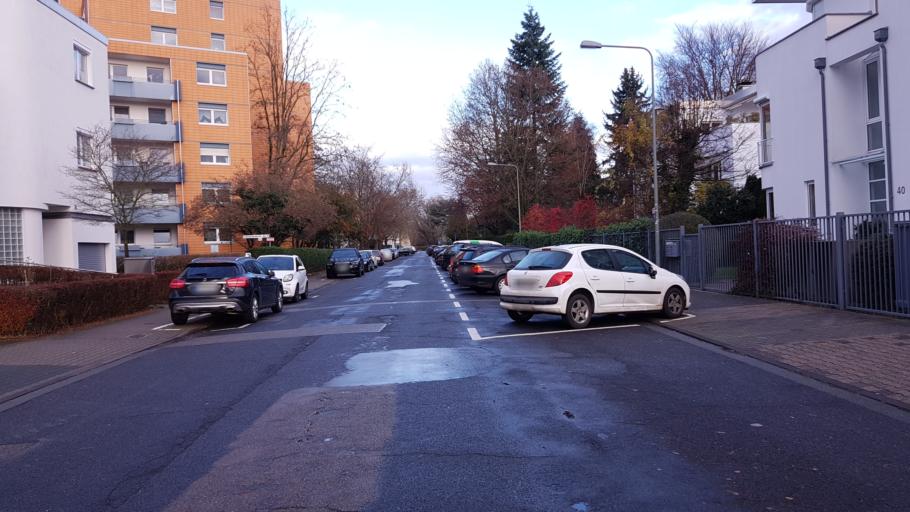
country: DE
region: Hesse
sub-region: Regierungsbezirk Darmstadt
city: Frankfurt am Main
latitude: 50.1405
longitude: 8.6644
